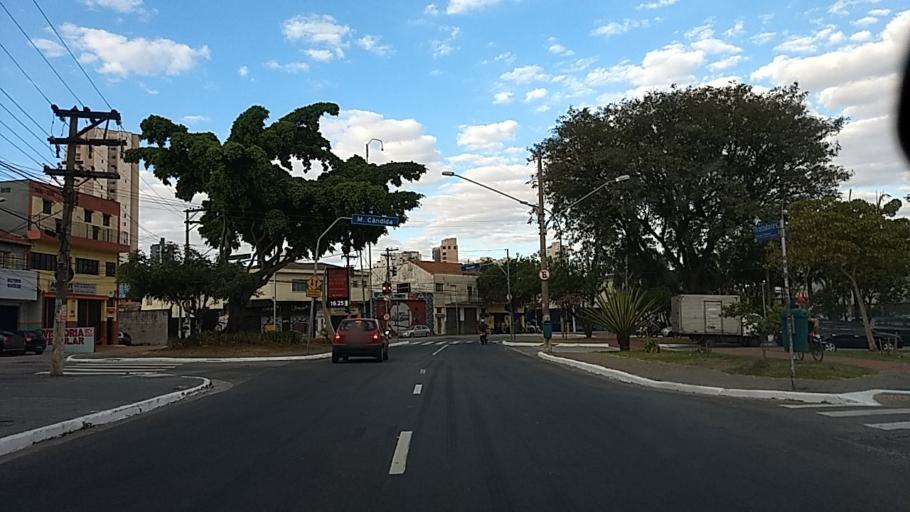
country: BR
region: Sao Paulo
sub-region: Sao Paulo
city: Sao Paulo
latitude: -23.5101
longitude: -46.5955
